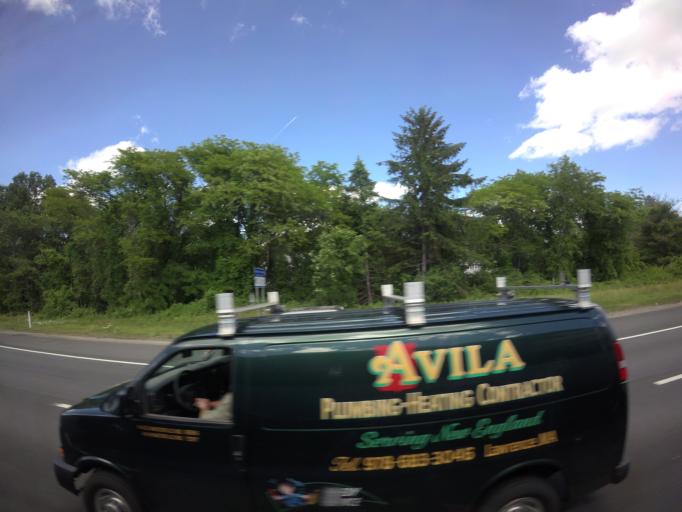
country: US
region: Massachusetts
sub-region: Middlesex County
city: Wilmington
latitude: 42.5730
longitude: -71.1491
